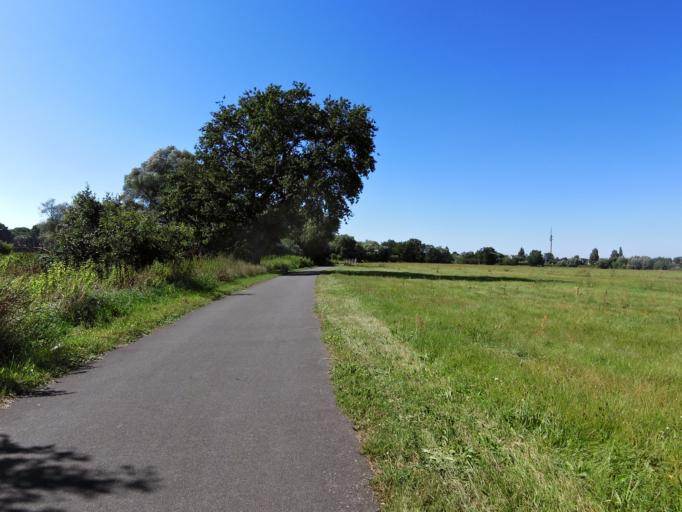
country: DE
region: Saxony-Anhalt
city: Abtsdorf
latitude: 51.8588
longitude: 12.6856
